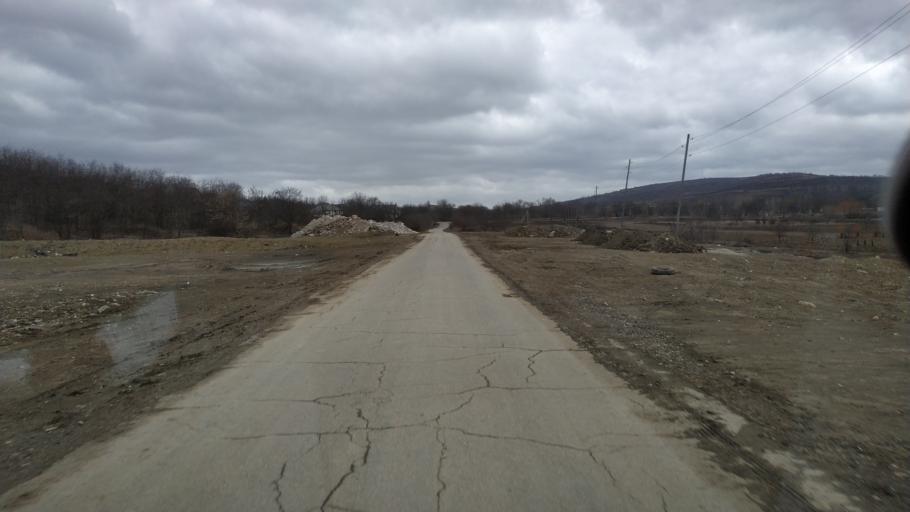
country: MD
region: Calarasi
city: Calarasi
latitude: 47.2448
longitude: 28.2911
